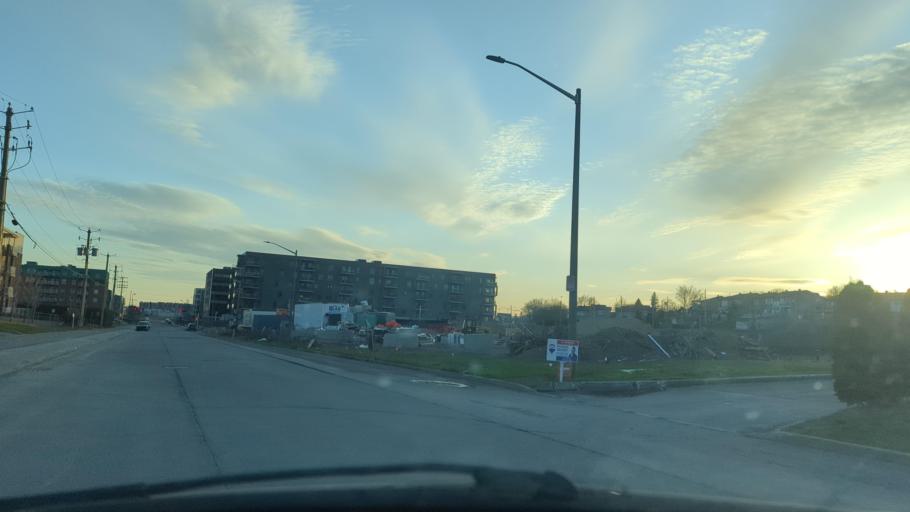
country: CA
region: Quebec
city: Quebec
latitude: 46.8474
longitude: -71.2644
